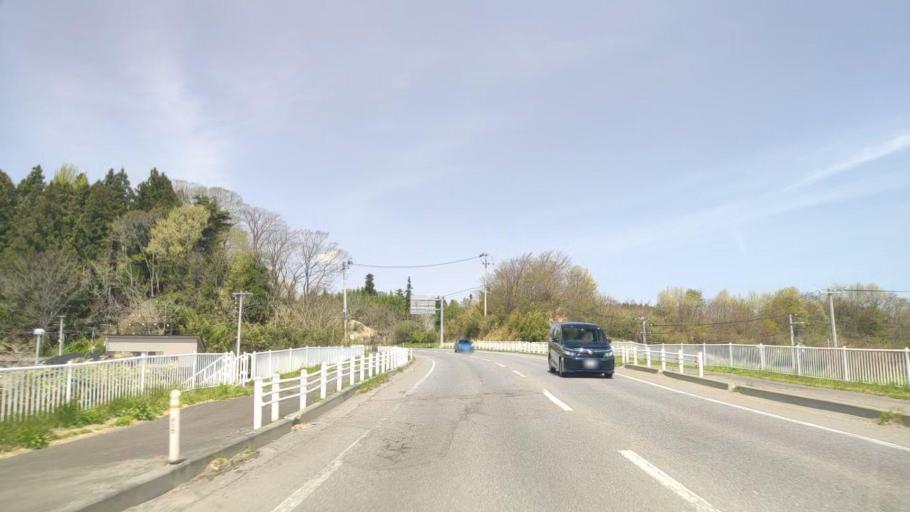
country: JP
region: Aomori
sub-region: Hachinohe Shi
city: Uchimaru
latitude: 40.5189
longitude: 141.4265
